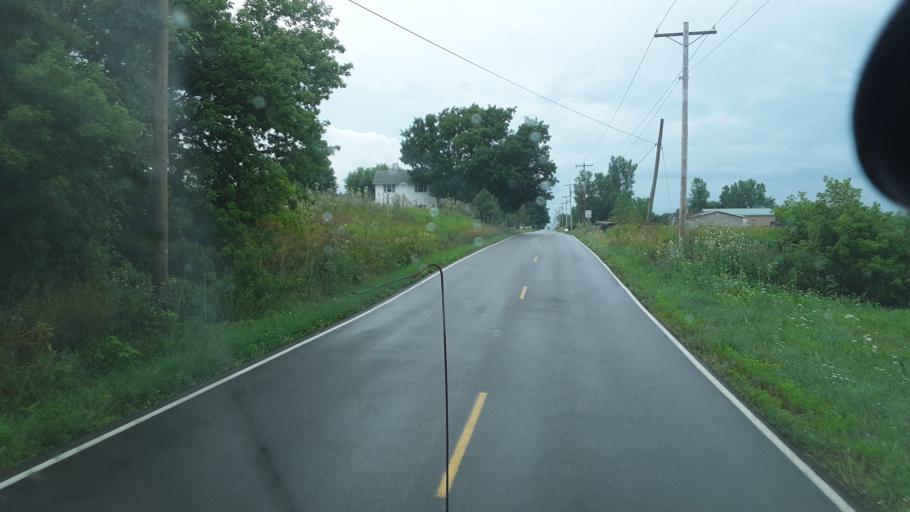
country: US
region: Indiana
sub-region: Steuben County
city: Hamilton
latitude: 41.6205
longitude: -84.8382
